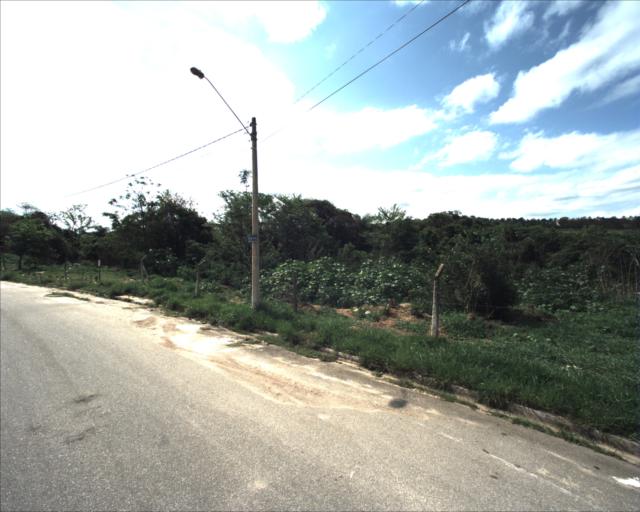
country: BR
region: Sao Paulo
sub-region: Sorocaba
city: Sorocaba
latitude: -23.3905
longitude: -47.3767
